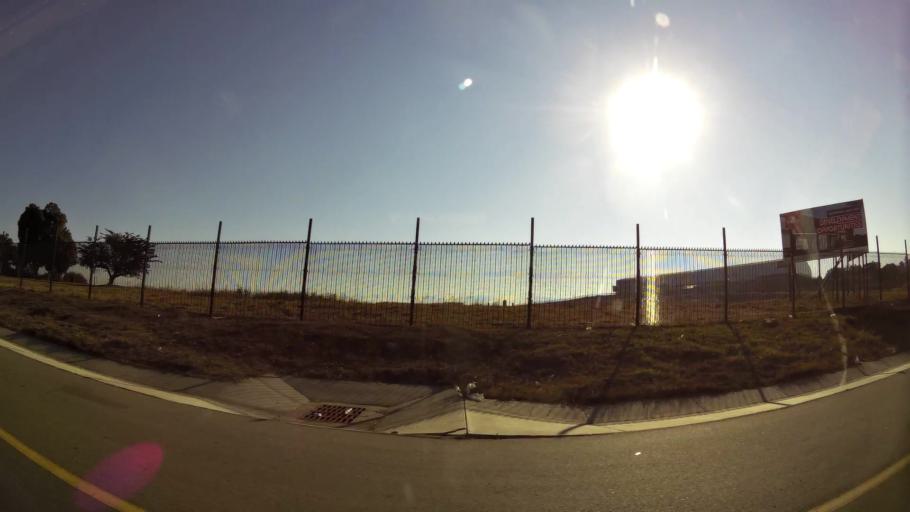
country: ZA
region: Gauteng
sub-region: City of Johannesburg Metropolitan Municipality
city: Modderfontein
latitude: -26.0572
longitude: 28.1683
